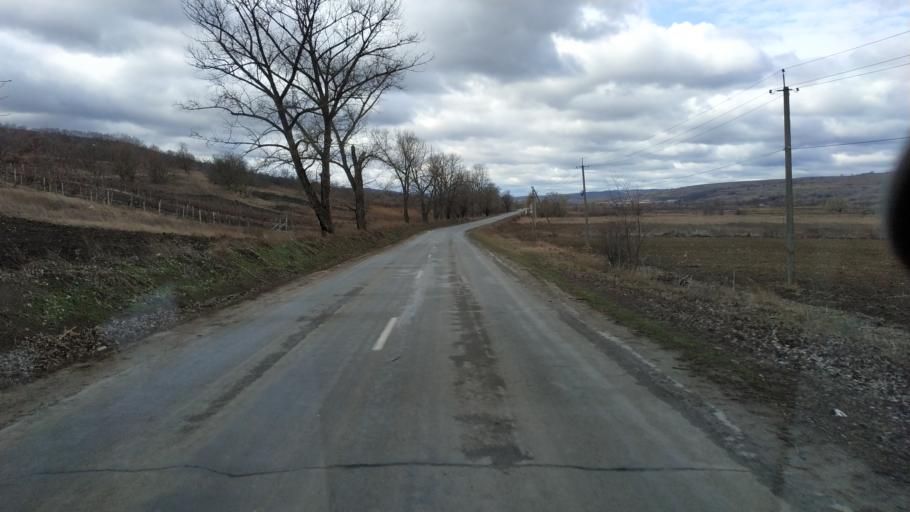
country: MD
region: Stinga Nistrului
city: Bucovat
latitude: 47.1507
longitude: 28.4165
